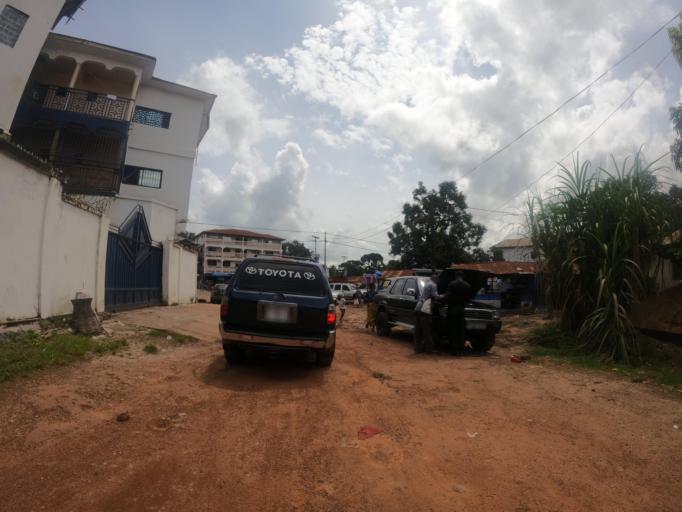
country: SL
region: Northern Province
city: Makeni
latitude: 8.8911
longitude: -12.0587
